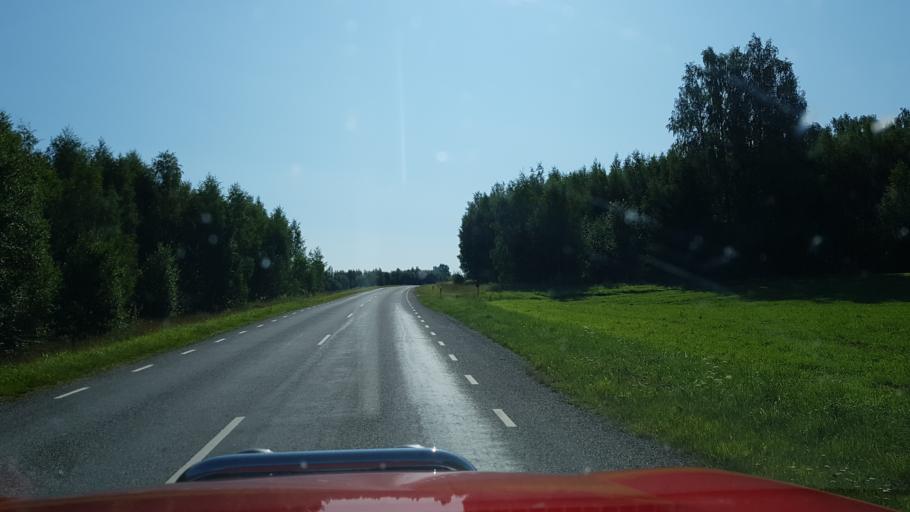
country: EE
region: Vorumaa
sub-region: Voru linn
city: Voru
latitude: 57.9765
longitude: 26.8169
